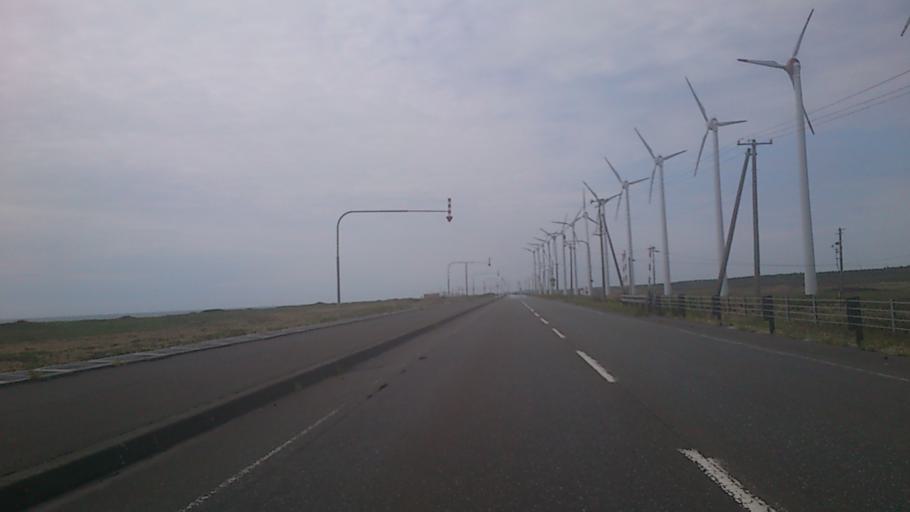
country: JP
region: Hokkaido
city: Makubetsu
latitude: 44.9685
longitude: 141.7006
